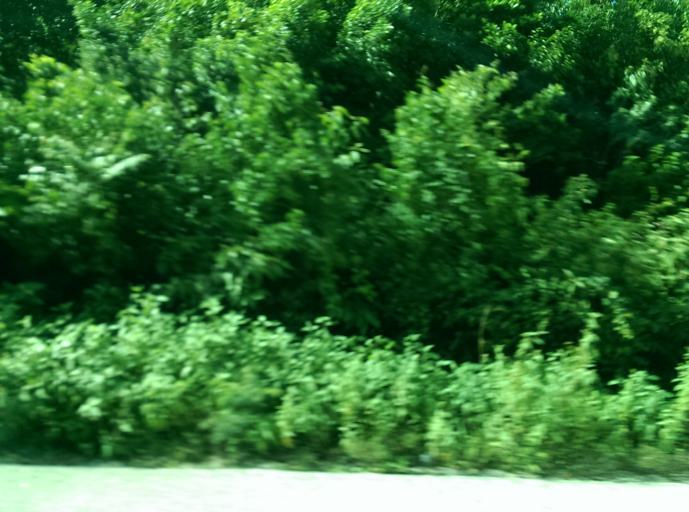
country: MX
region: Quintana Roo
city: Tulum
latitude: 20.2235
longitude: -87.4567
